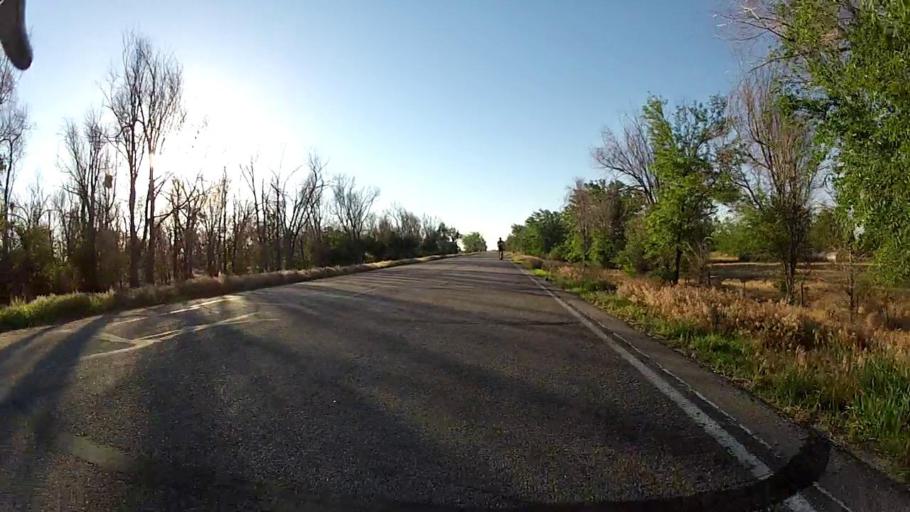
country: US
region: Kansas
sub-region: Ford County
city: Dodge City
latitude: 37.7122
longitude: -99.9234
